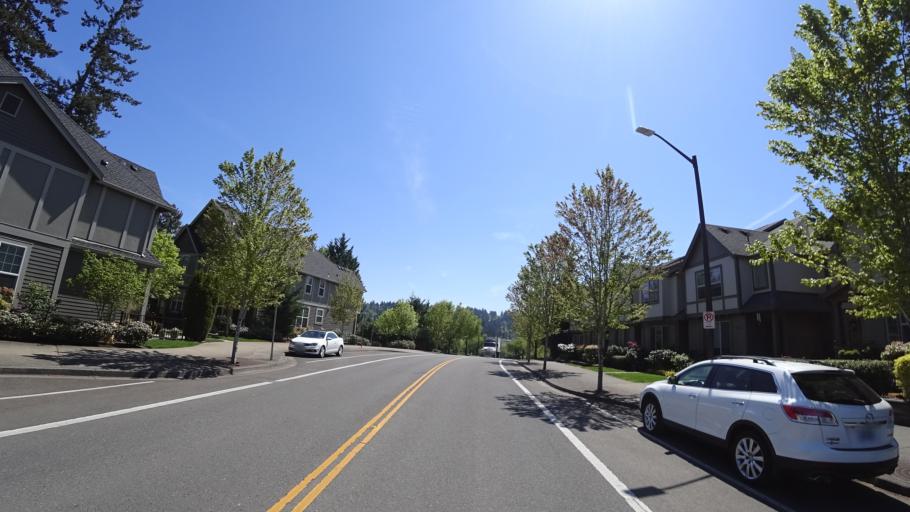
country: US
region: Oregon
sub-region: Washington County
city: King City
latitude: 45.4334
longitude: -122.8320
